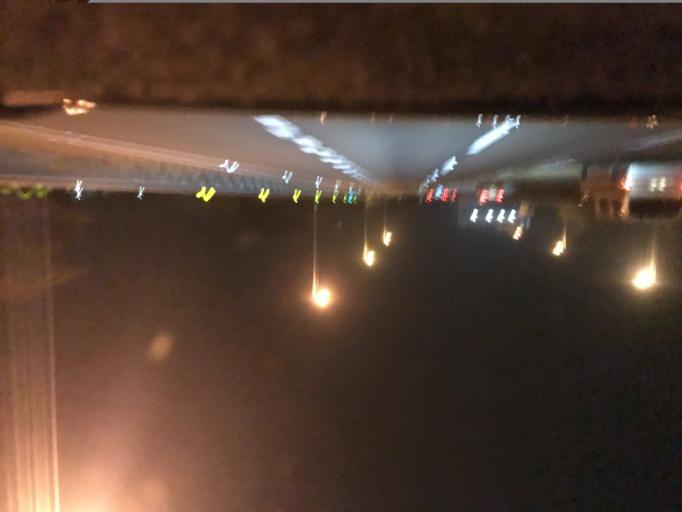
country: TW
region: Taiwan
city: Fengyuan
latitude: 24.3389
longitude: 120.6482
